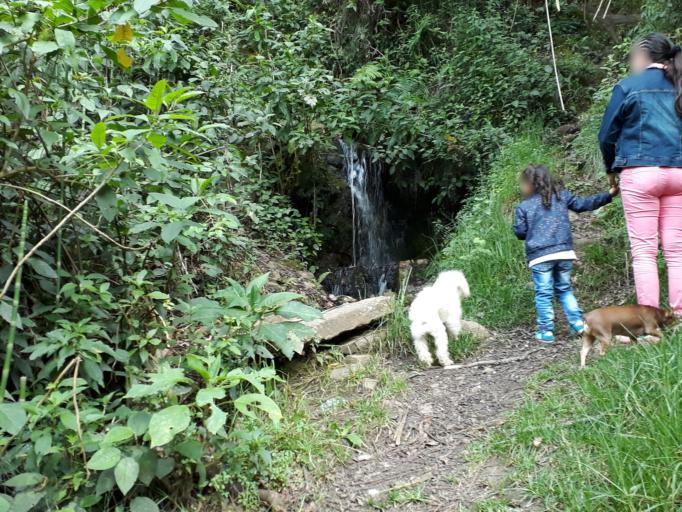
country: CO
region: Boyaca
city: Santa Rosa de Viterbo
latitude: 5.8590
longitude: -72.9711
